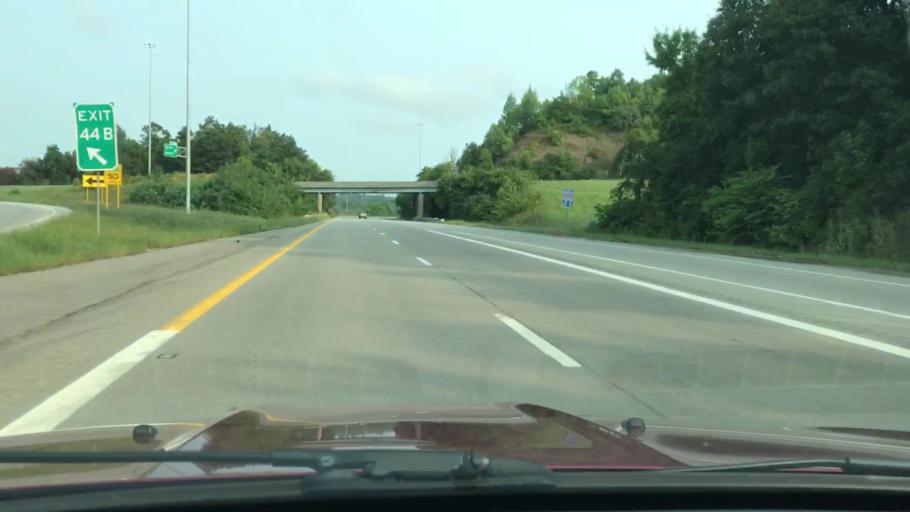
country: US
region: Ohio
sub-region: Guernsey County
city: Byesville
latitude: 39.9987
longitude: -81.5564
